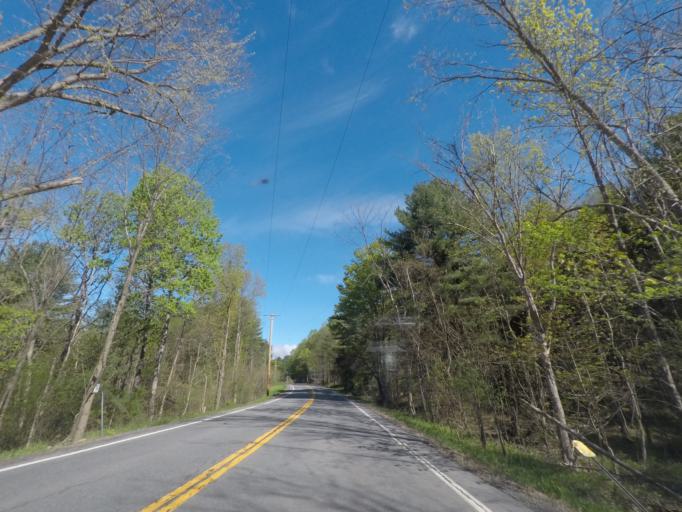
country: US
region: New York
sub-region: Albany County
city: Ravena
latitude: 42.4988
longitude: -73.9442
